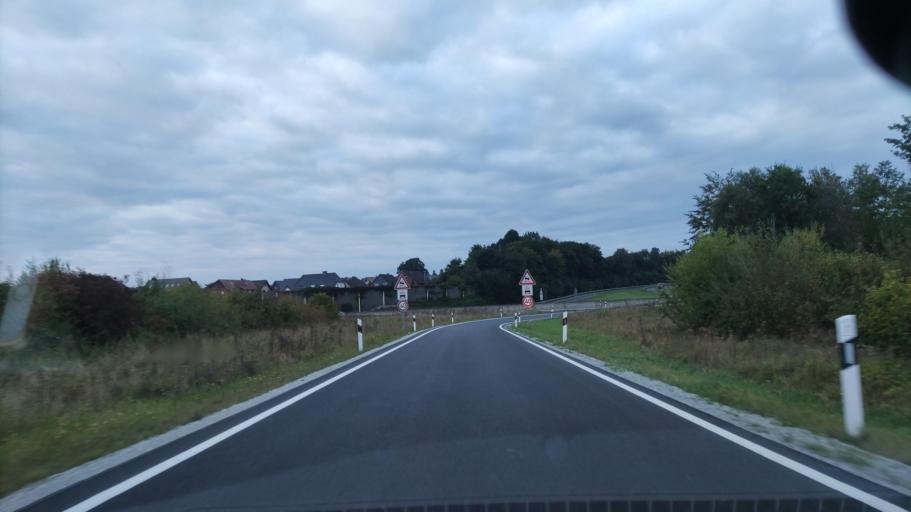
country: DE
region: Lower Saxony
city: Wallenhorst
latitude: 52.3393
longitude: 8.0187
